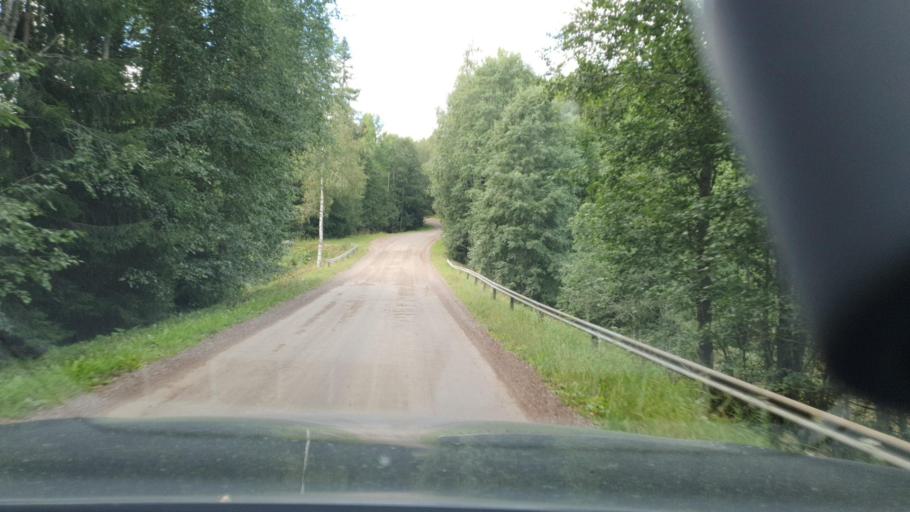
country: SE
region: Vaermland
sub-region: Filipstads Kommun
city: Filipstad
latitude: 59.5424
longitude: 13.9709
